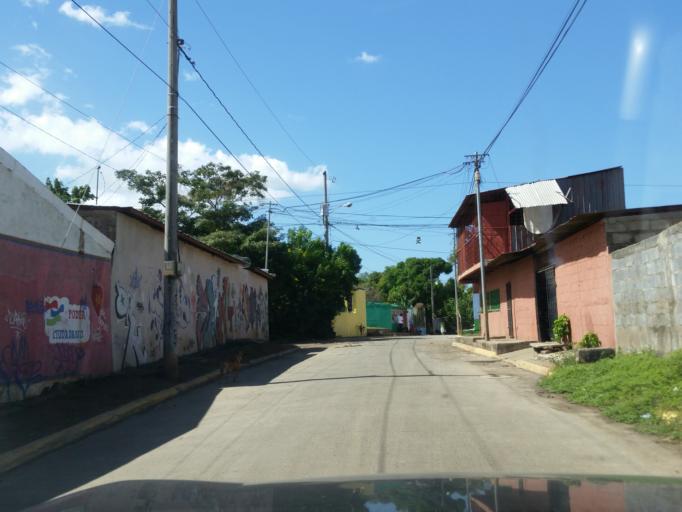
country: NI
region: Managua
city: Managua
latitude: 12.1198
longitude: -86.2261
